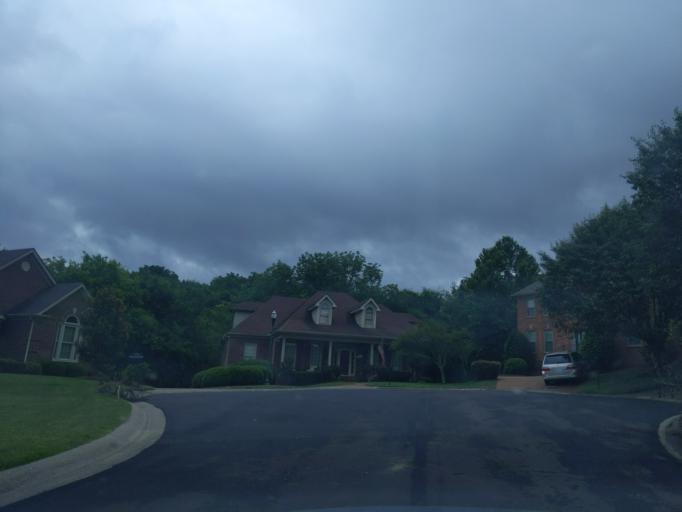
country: US
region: Tennessee
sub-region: Williamson County
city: Brentwood Estates
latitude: 36.0377
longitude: -86.7524
